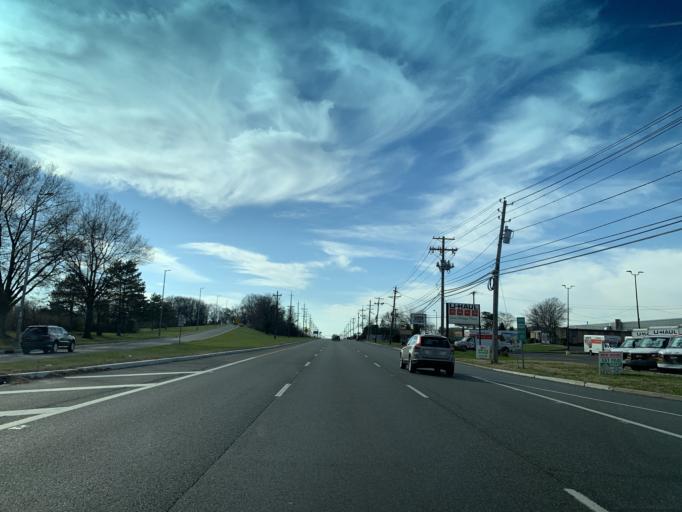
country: US
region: New Jersey
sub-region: Burlington County
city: Palmyra
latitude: 39.9790
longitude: -75.0275
